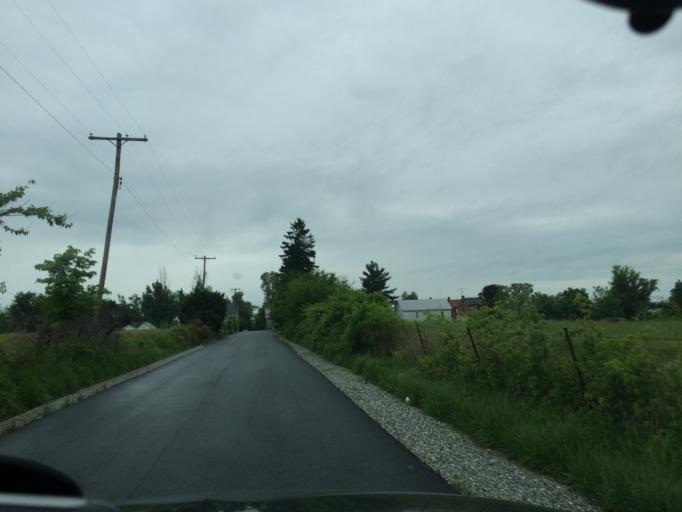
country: US
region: Maryland
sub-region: Carroll County
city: Taneytown
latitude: 39.5931
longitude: -77.2206
